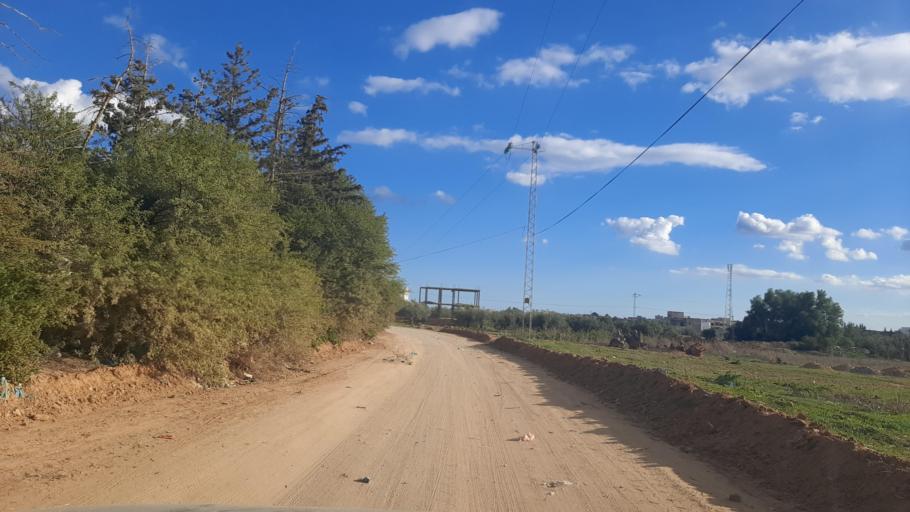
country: TN
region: Nabul
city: Al Hammamat
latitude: 36.4205
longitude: 10.5109
